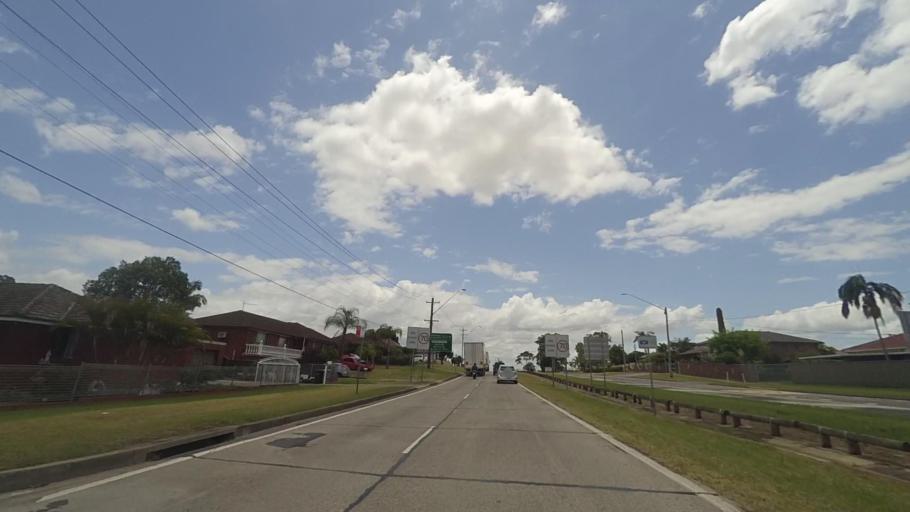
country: AU
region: New South Wales
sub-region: Fairfield
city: Fairfield Heights
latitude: -33.8663
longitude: 150.9258
